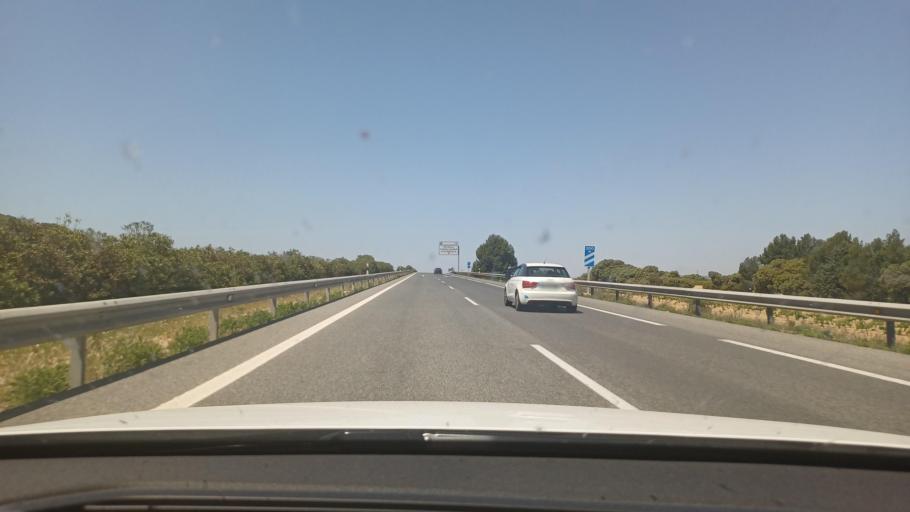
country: ES
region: Castille-La Mancha
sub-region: Provincia de Albacete
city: Corral-Rubio
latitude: 38.9004
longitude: -1.4793
